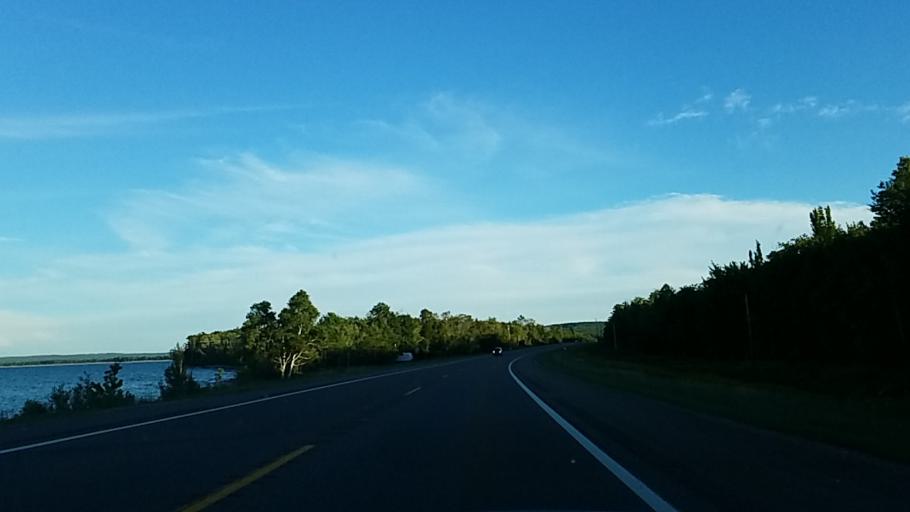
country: US
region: Michigan
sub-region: Alger County
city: Munising
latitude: 46.4555
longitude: -86.8902
